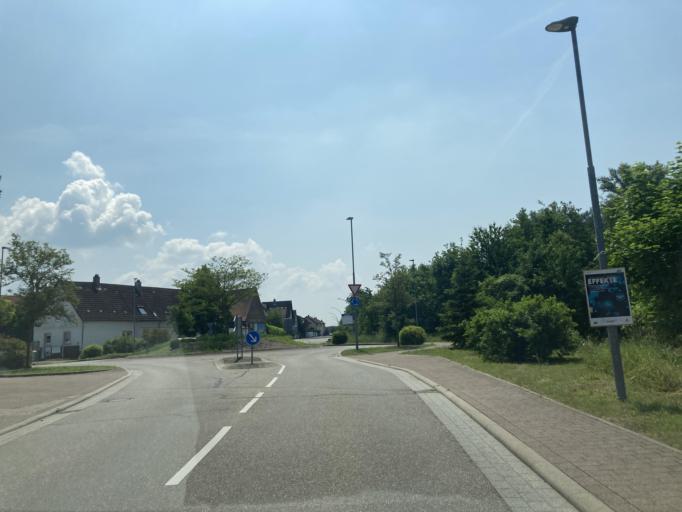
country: DE
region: Baden-Wuerttemberg
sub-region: Karlsruhe Region
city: Linkenheim-Hochstetten
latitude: 49.1392
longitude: 8.4086
